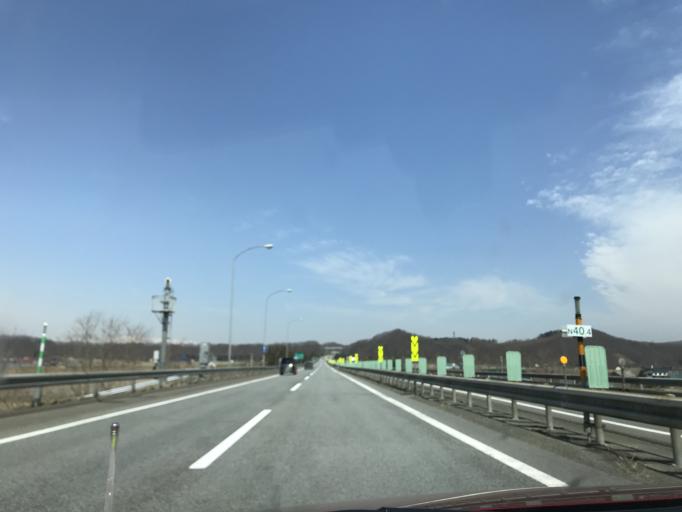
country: JP
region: Hokkaido
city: Iwamizawa
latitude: 43.2311
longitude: 141.8305
